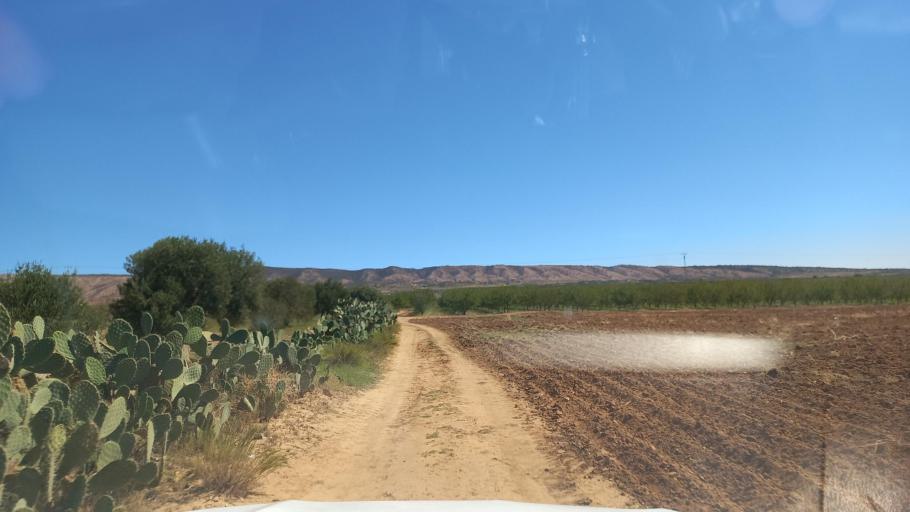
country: TN
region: Al Qasrayn
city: Sbiba
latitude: 35.3468
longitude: 9.1066
